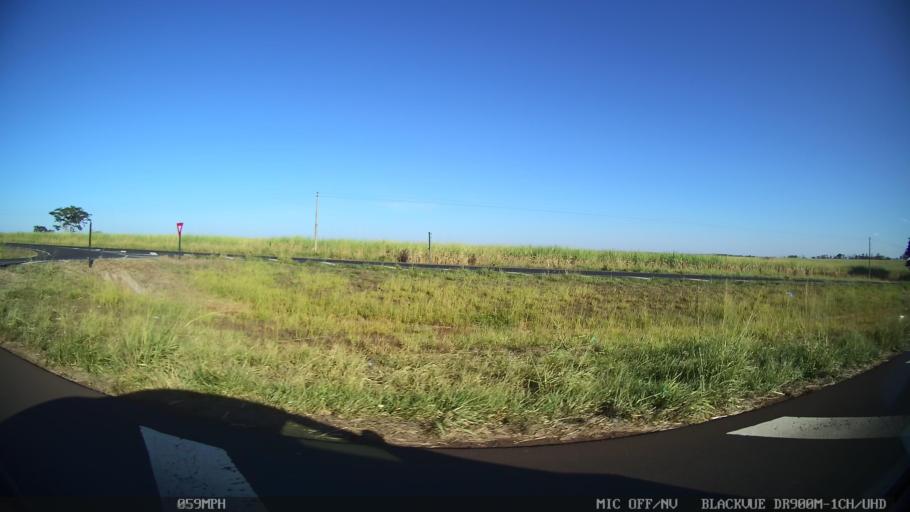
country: BR
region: Sao Paulo
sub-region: Olimpia
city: Olimpia
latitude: -20.7249
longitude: -49.0320
